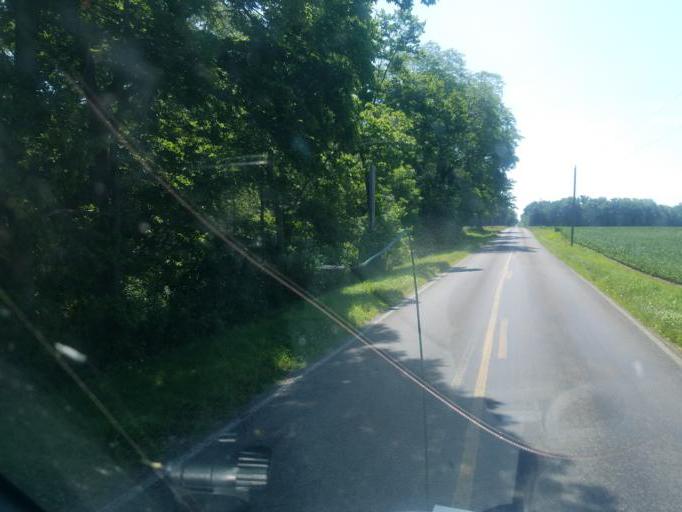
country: US
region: Ohio
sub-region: Champaign County
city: North Lewisburg
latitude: 40.2223
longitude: -83.5205
